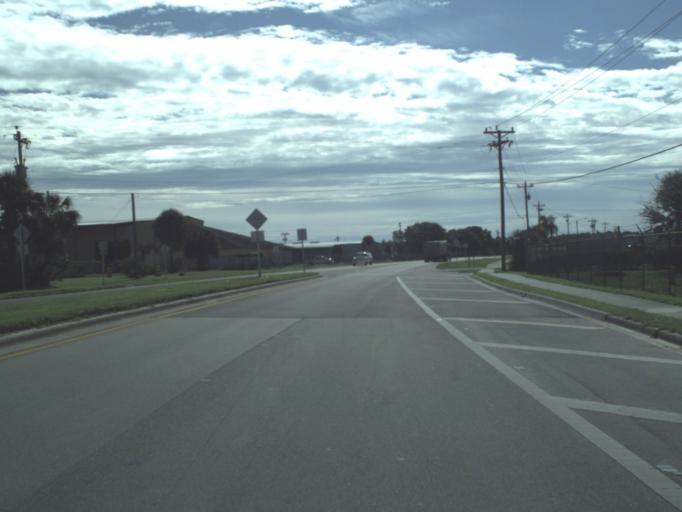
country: US
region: Florida
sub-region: Collier County
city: Immokalee
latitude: 26.4177
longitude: -81.4084
